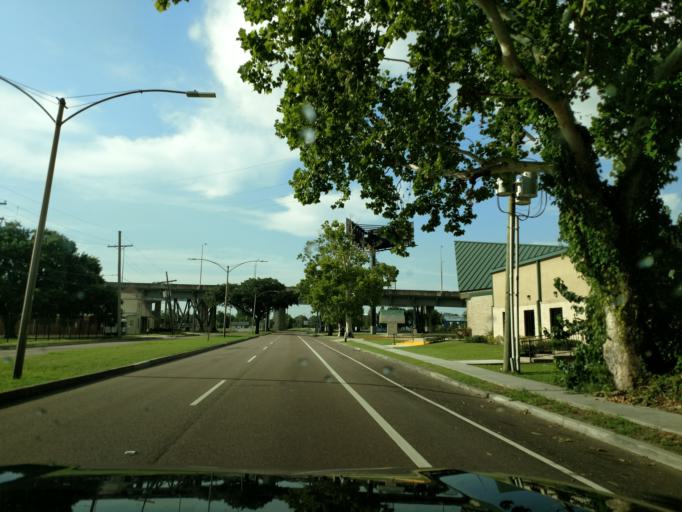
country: US
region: Louisiana
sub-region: Jefferson Parish
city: Gretna
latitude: 29.9362
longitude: -90.0414
